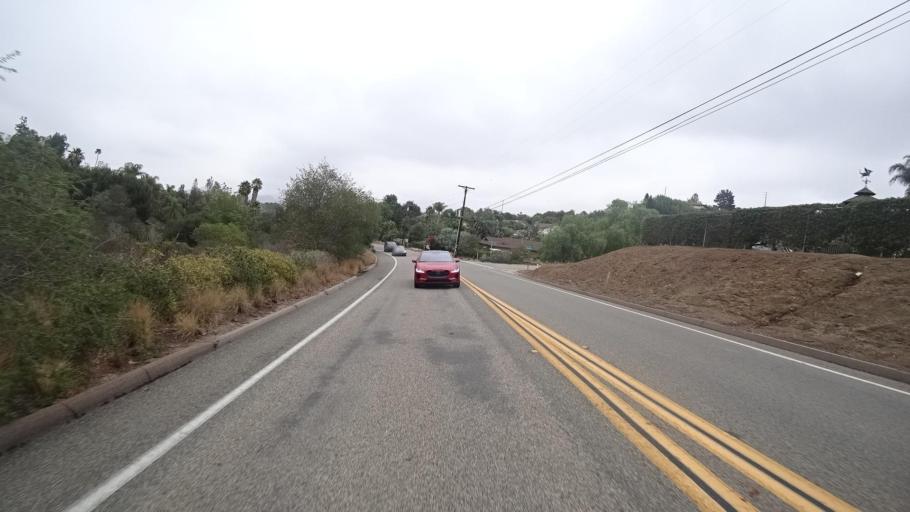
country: US
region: California
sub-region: San Diego County
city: Escondido
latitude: 33.0751
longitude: -117.0927
